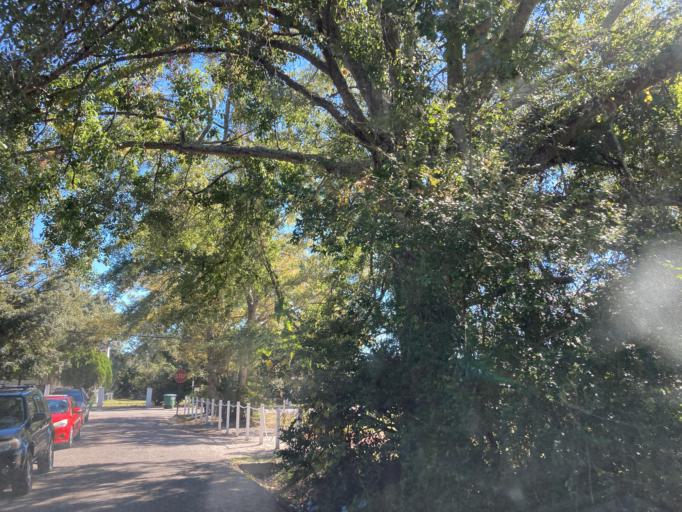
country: US
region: Mississippi
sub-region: Jackson County
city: Ocean Springs
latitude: 30.4142
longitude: -88.8193
